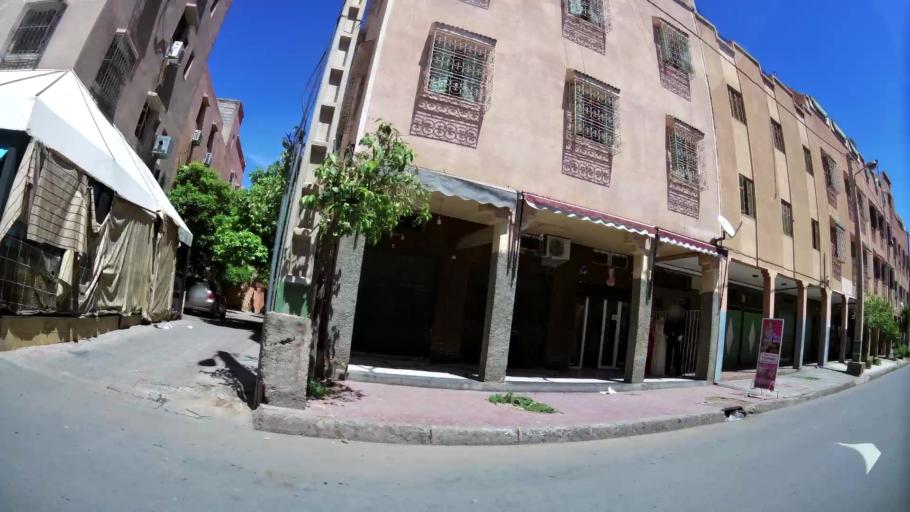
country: MA
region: Marrakech-Tensift-Al Haouz
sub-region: Marrakech
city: Marrakesh
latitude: 31.6311
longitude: -8.0523
